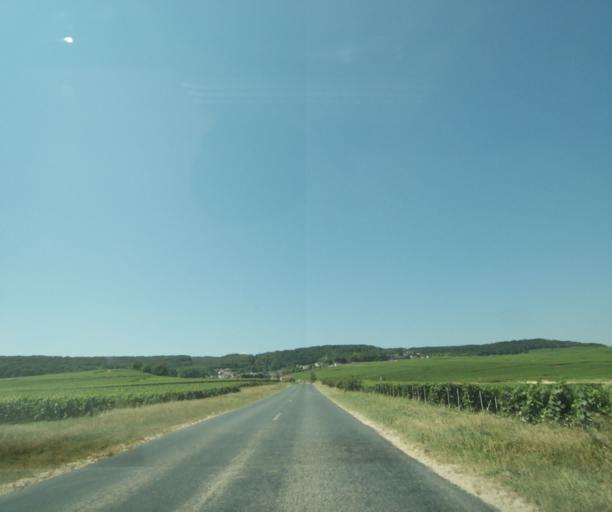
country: FR
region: Champagne-Ardenne
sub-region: Departement de la Marne
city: Verzy
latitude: 49.1519
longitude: 4.1778
